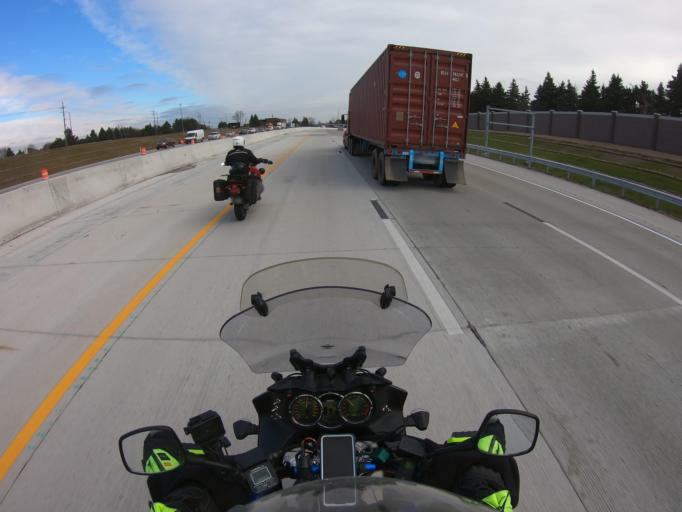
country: US
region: Michigan
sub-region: Oakland County
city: Troy
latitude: 42.6040
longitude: -83.1754
